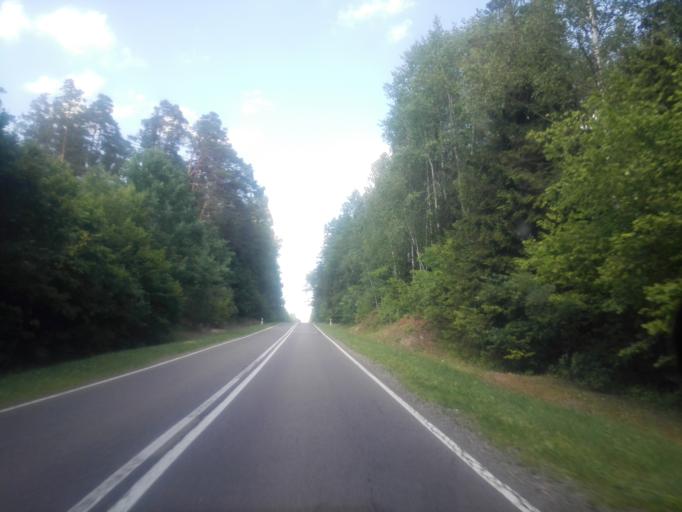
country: PL
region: Podlasie
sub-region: Powiat sejnenski
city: Sejny
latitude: 54.0120
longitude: 23.3310
